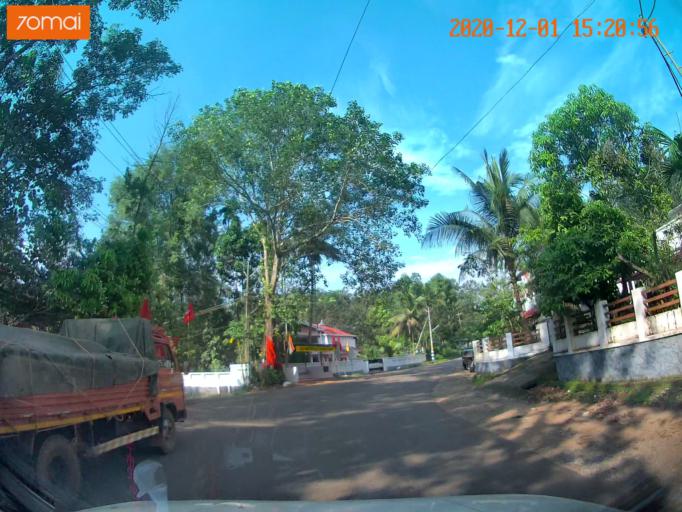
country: IN
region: Kerala
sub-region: Ernakulam
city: Ramamangalam
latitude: 9.9457
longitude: 76.5393
